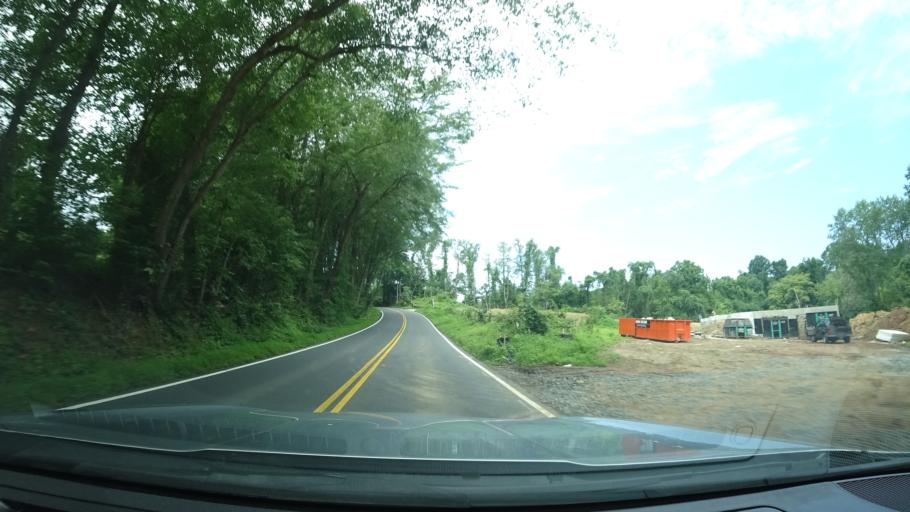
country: US
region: Virginia
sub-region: Fairfax County
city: Great Falls
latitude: 38.9832
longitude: -77.2884
